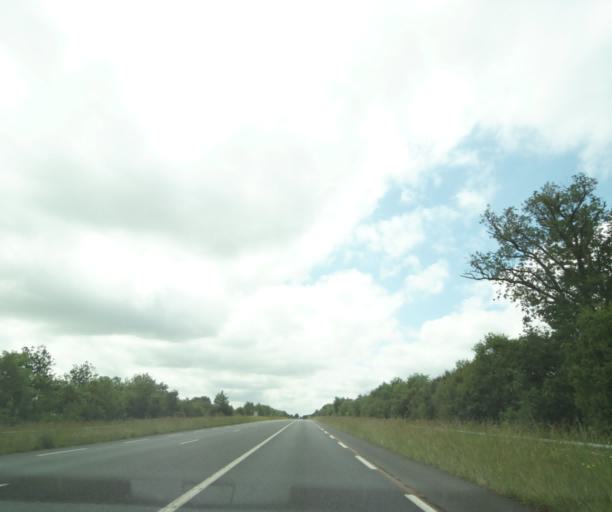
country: FR
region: Poitou-Charentes
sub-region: Departement des Deux-Sevres
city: Airvault
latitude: 46.7843
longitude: -0.2167
